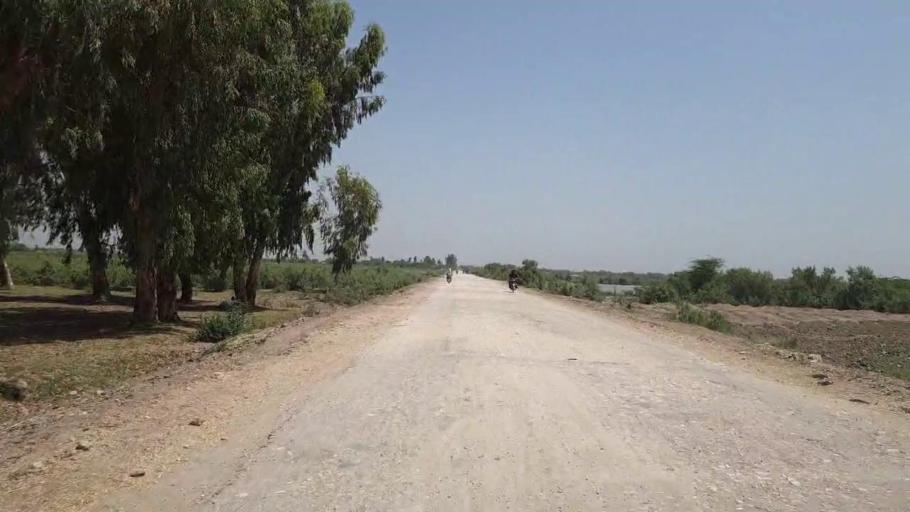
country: PK
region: Sindh
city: Adilpur
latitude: 27.8975
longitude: 69.2910
